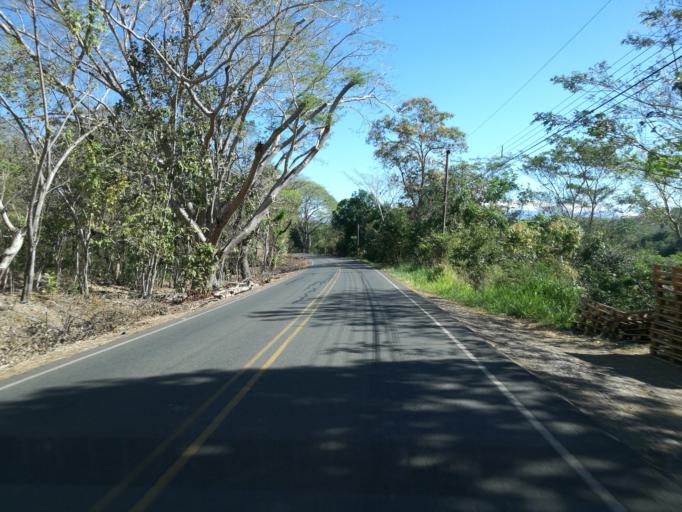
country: CR
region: Puntarenas
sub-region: Canton Central de Puntarenas
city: Puntarenas
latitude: 10.0939
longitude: -84.9205
